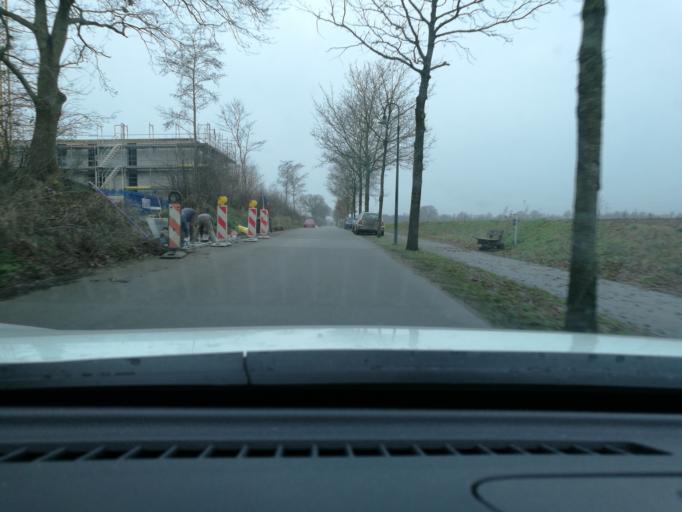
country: DE
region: Schleswig-Holstein
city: Borgstedt
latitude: 54.3346
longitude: 9.7036
